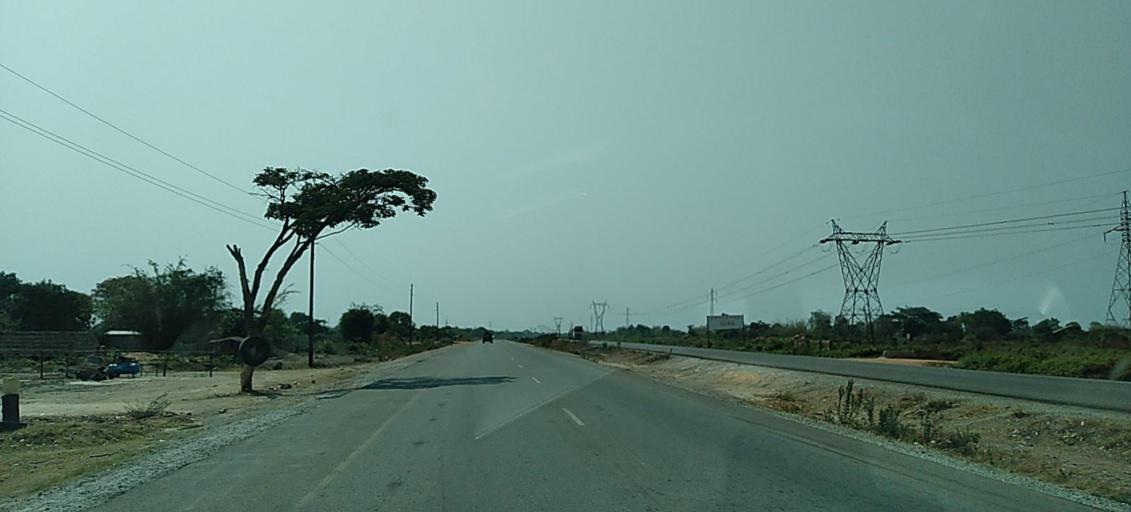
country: ZM
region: Copperbelt
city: Chambishi
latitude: -12.6003
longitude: 27.9646
